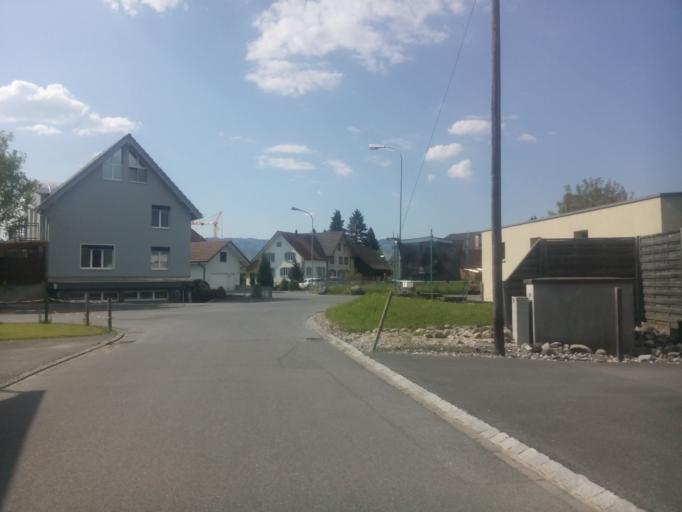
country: AT
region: Vorarlberg
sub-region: Politischer Bezirk Feldkirch
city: Koblach
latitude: 47.3308
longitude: 9.5859
